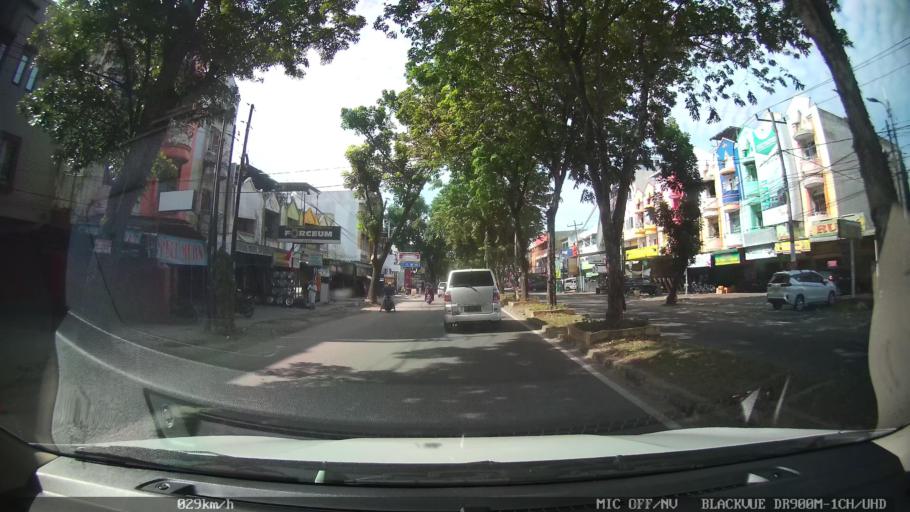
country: ID
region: North Sumatra
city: Medan
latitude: 3.5810
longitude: 98.6432
